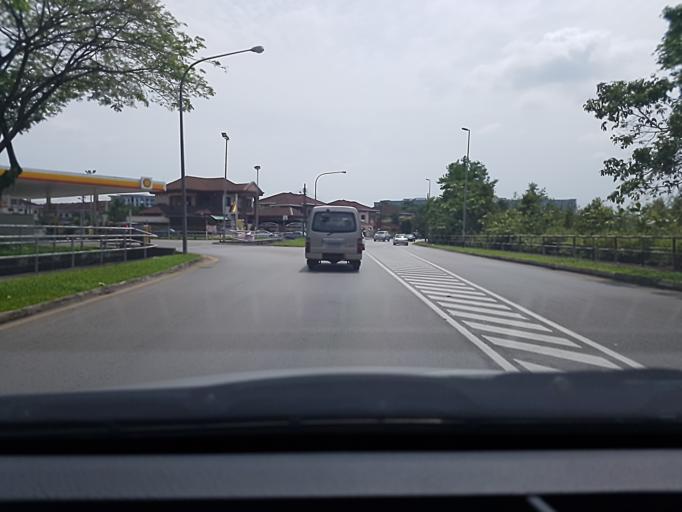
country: MY
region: Sarawak
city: Kuching
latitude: 1.5180
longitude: 110.3677
